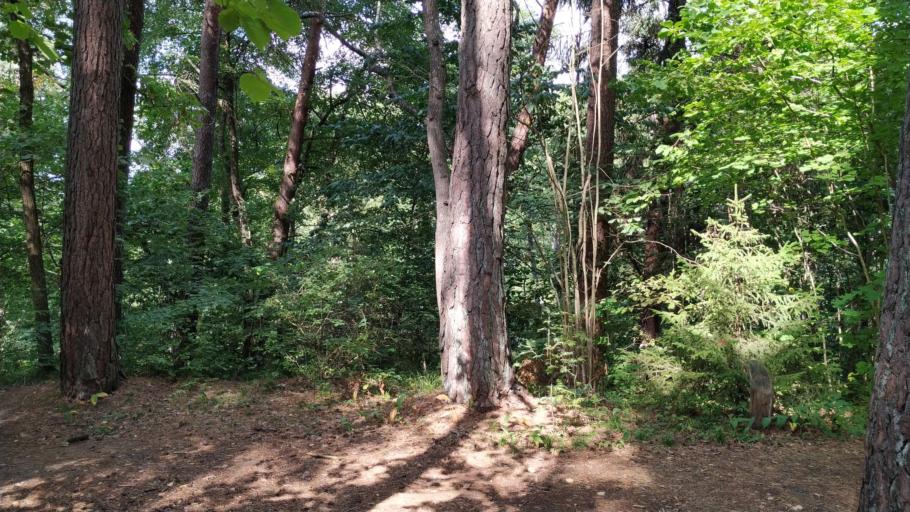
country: LT
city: Grigiskes
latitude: 54.7990
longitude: 24.9811
